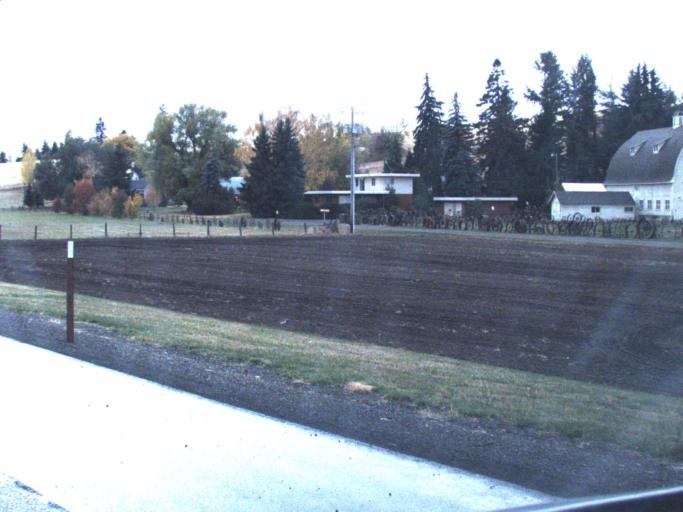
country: US
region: Washington
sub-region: Asotin County
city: Clarkston
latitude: 46.5453
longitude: -117.0918
